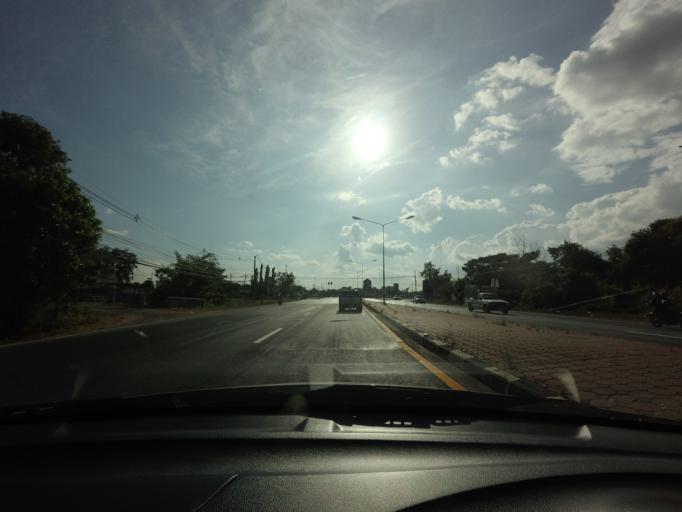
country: TH
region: Nakhon Nayok
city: Nakhon Nayok
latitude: 14.2210
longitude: 101.2300
